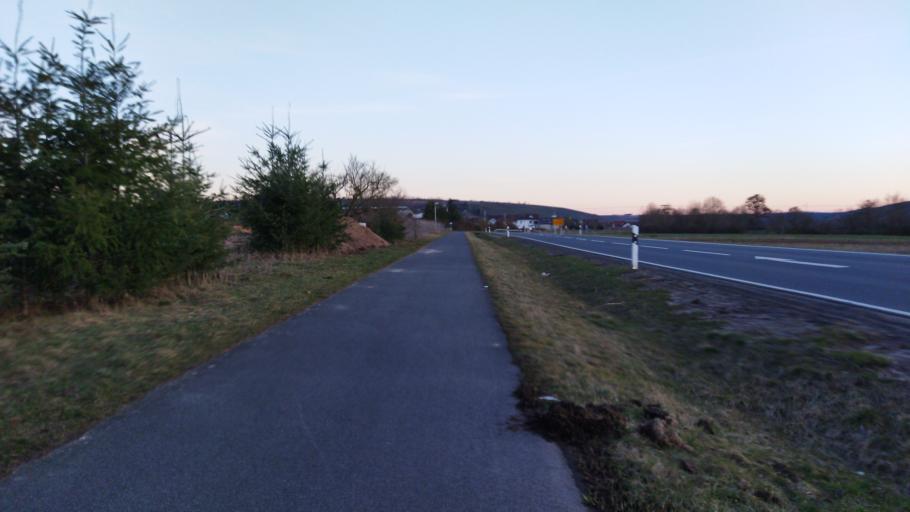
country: DE
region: Bavaria
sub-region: Regierungsbezirk Unterfranken
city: Wipfeld
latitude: 49.9155
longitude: 10.1902
